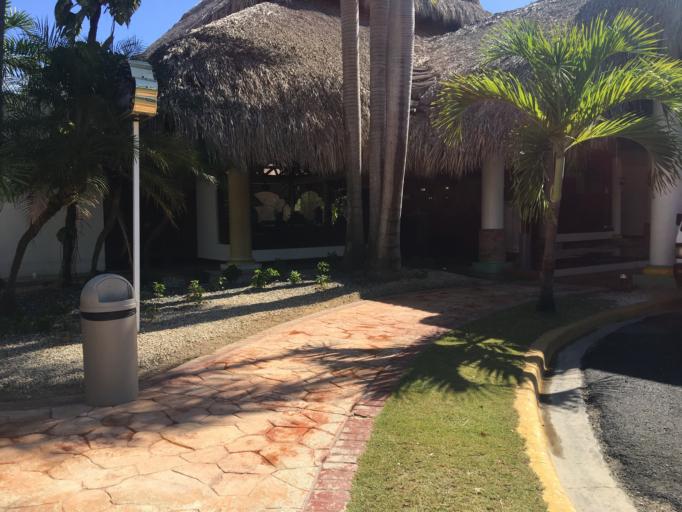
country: DO
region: San Juan
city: Punta Cana
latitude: 18.7083
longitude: -68.4439
